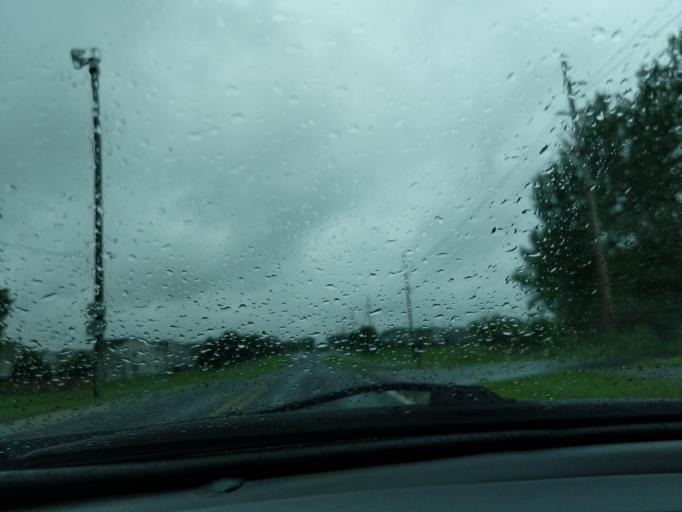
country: US
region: Indiana
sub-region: Hamilton County
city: Noblesville
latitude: 40.0649
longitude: -86.0335
